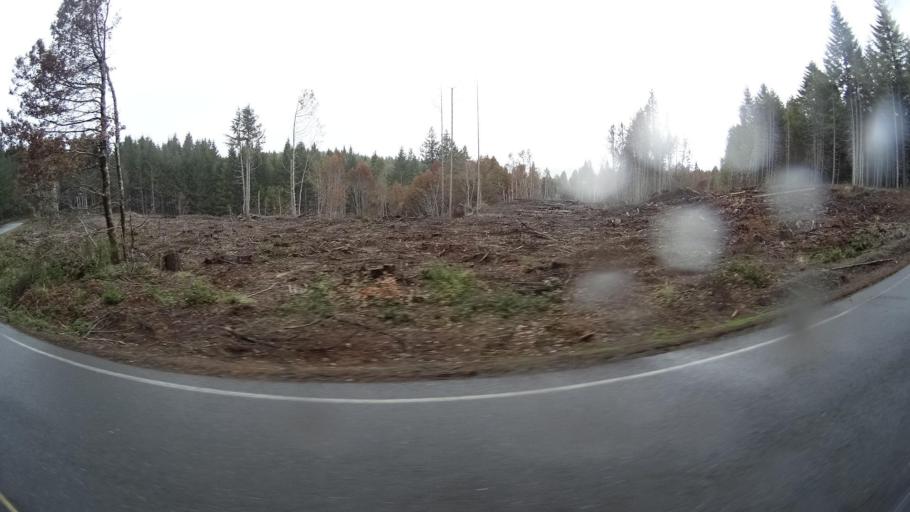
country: US
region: California
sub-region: Humboldt County
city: Willow Creek
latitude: 41.1745
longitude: -123.8147
